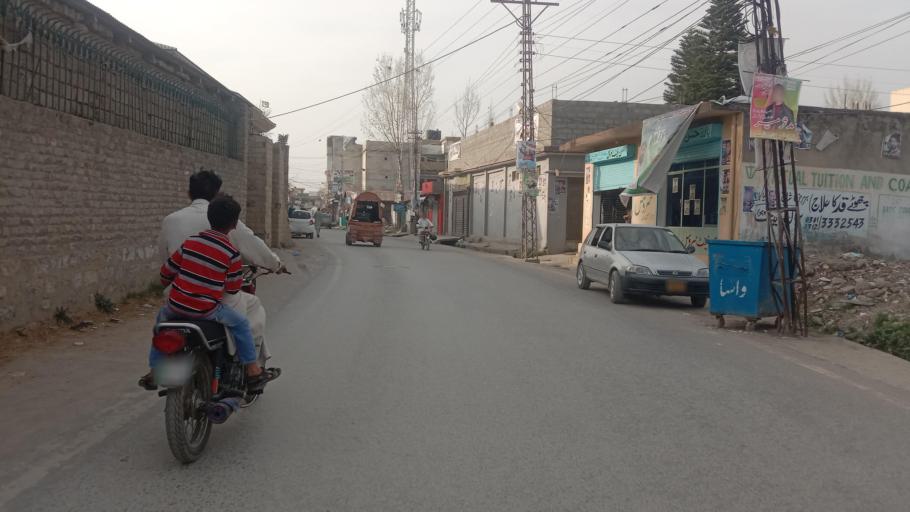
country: PK
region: Khyber Pakhtunkhwa
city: Abbottabad
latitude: 34.1612
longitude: 73.2630
